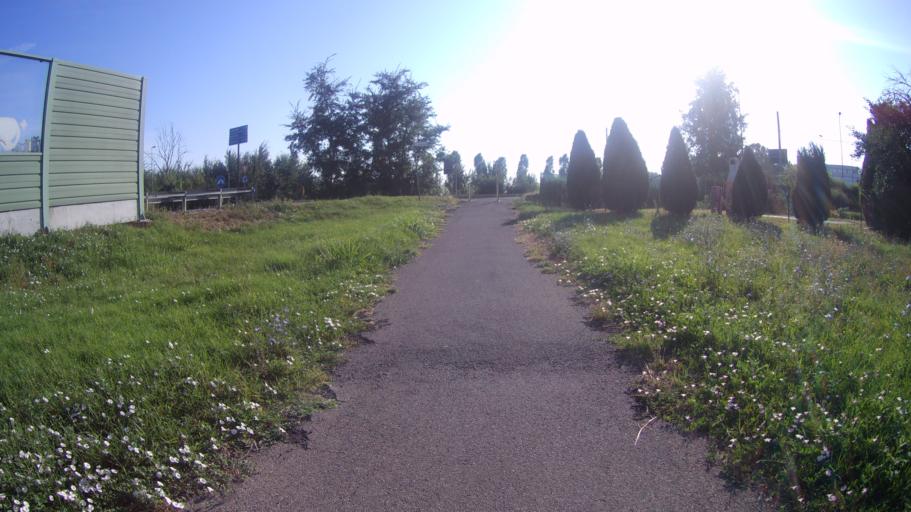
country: IT
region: Emilia-Romagna
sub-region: Provincia di Reggio Emilia
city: Fogliano
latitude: 44.6807
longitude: 10.6832
